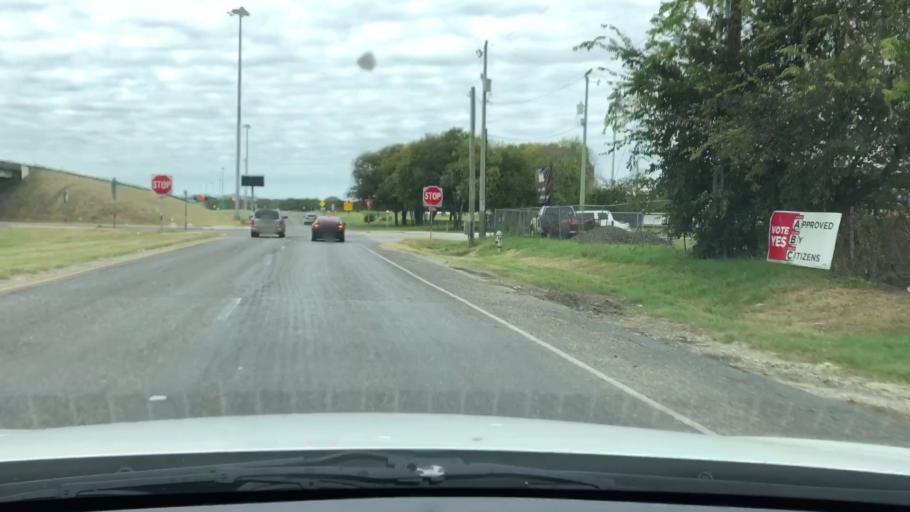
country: US
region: Texas
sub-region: Bexar County
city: Lackland Air Force Base
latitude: 29.4077
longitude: -98.5991
